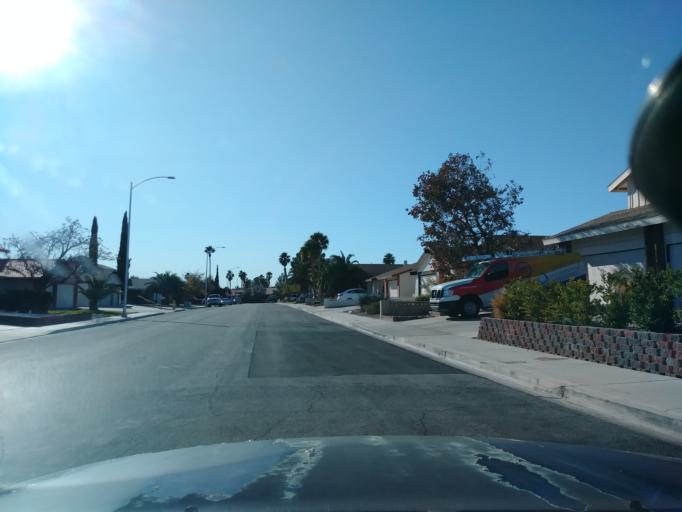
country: US
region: Nevada
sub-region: Clark County
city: Spring Valley
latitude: 36.1499
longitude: -115.2325
